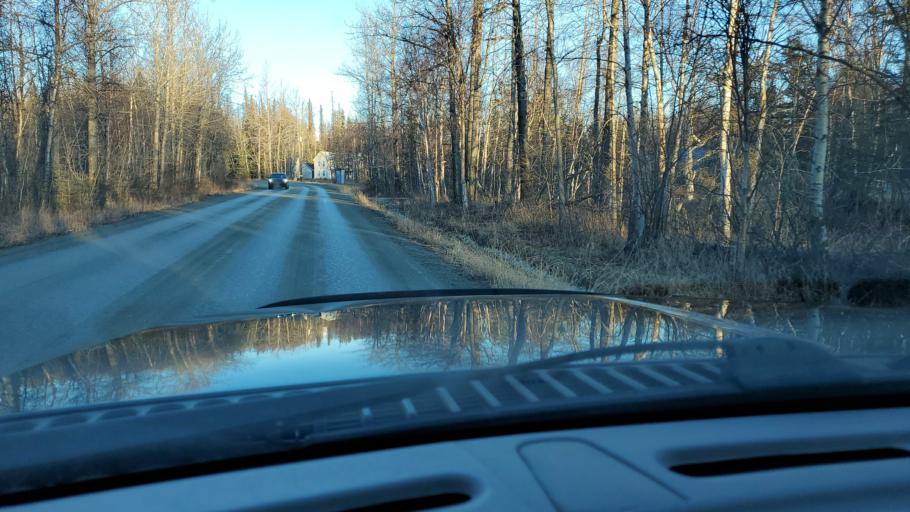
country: US
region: Alaska
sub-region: Matanuska-Susitna Borough
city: Gateway
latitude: 61.5893
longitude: -149.2457
